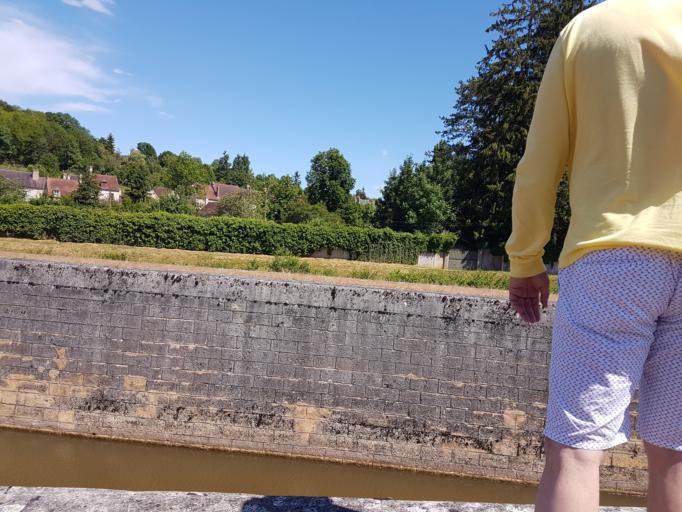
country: FR
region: Bourgogne
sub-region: Departement de la Nievre
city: Clamecy
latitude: 47.4584
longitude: 3.5229
